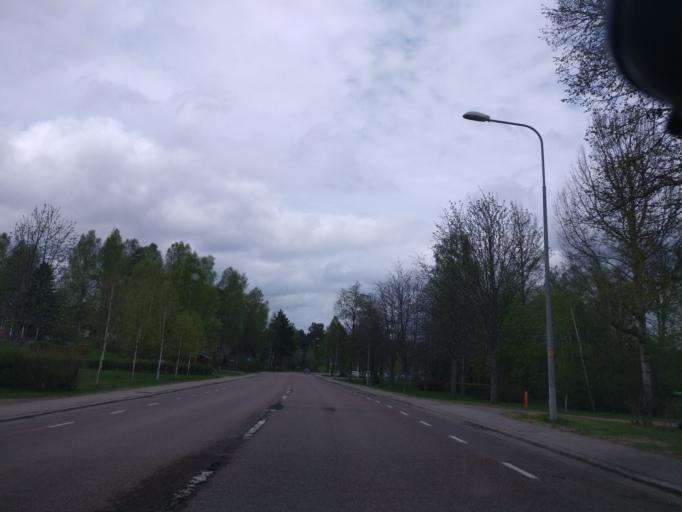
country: SE
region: Vaermland
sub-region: Hagfors Kommun
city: Ekshaerad
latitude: 60.1798
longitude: 13.4962
